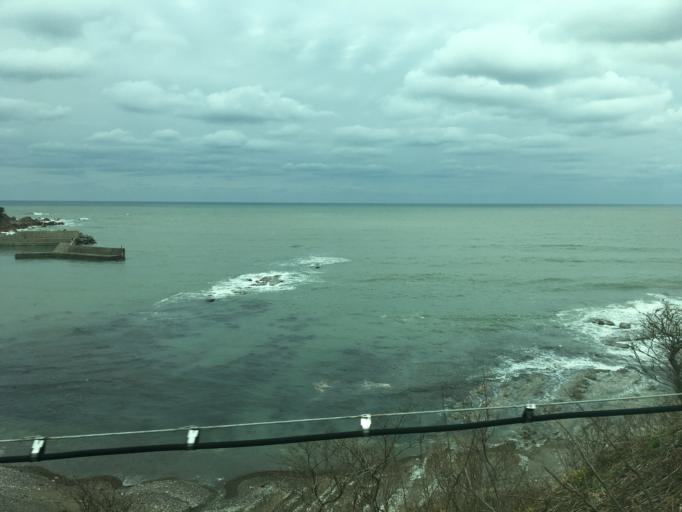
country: JP
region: Aomori
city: Shimokizukuri
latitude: 40.6675
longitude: 139.9437
